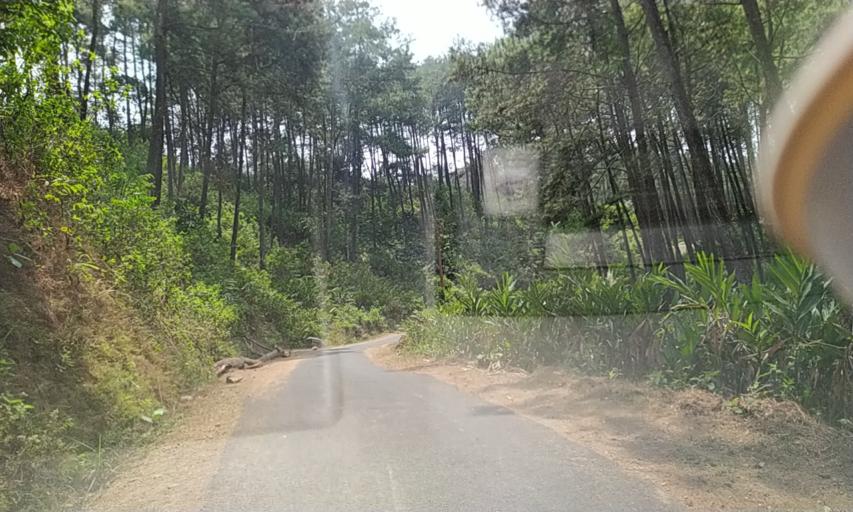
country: ID
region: Central Java
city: Jambuluwuk
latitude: -7.3294
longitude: 108.9316
